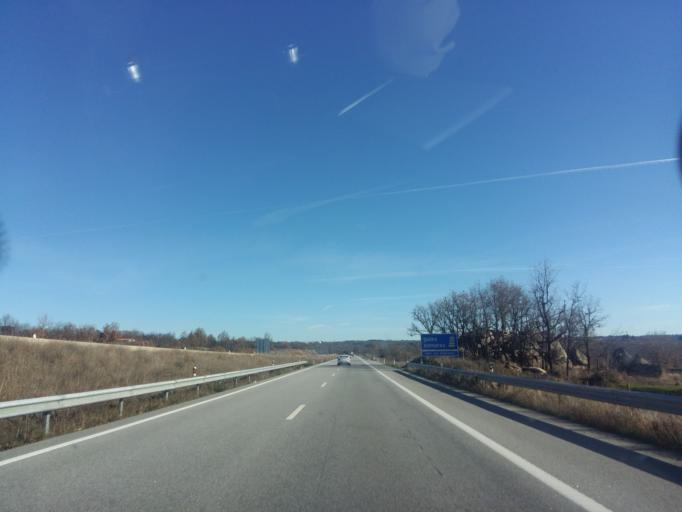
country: PT
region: Guarda
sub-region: Pinhel
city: Pinhel
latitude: 40.6038
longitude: -7.0552
